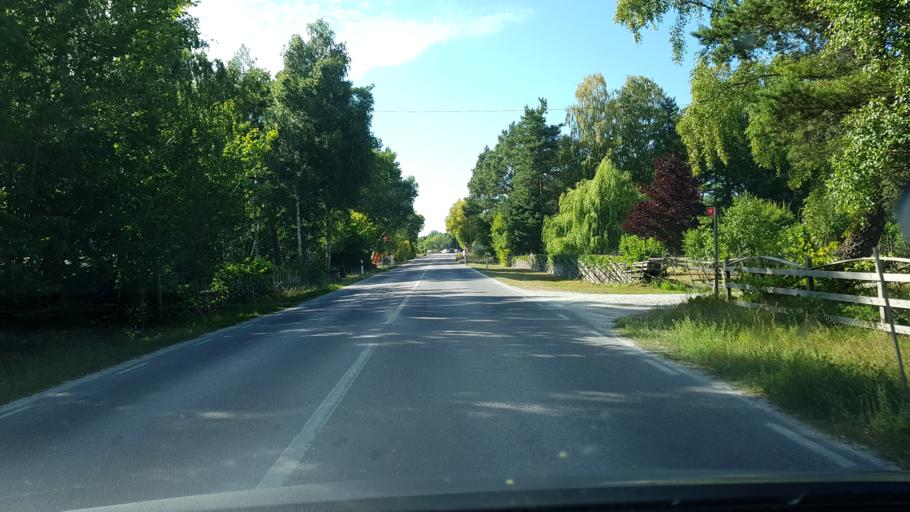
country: SE
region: Gotland
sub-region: Gotland
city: Klintehamn
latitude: 57.4076
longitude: 18.1683
